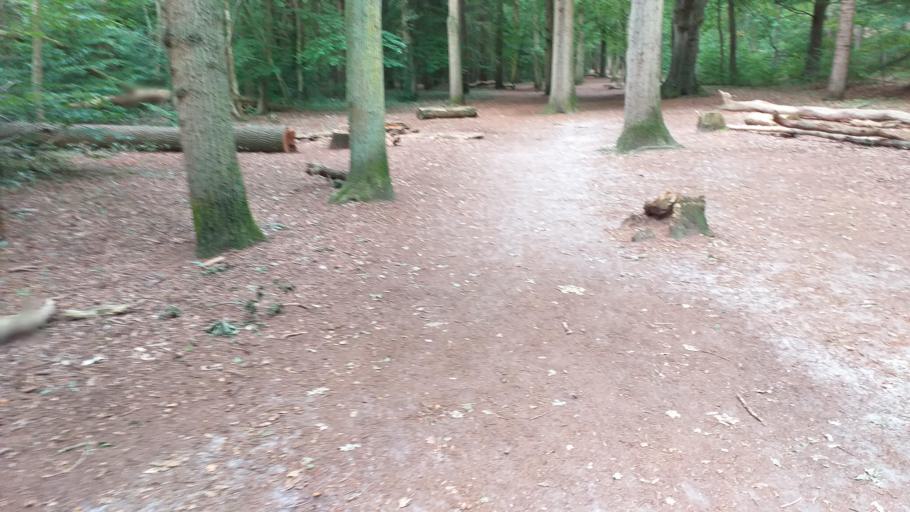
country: NL
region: North Holland
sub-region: Gemeente Heiloo
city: Heiloo
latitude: 52.6745
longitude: 4.6881
